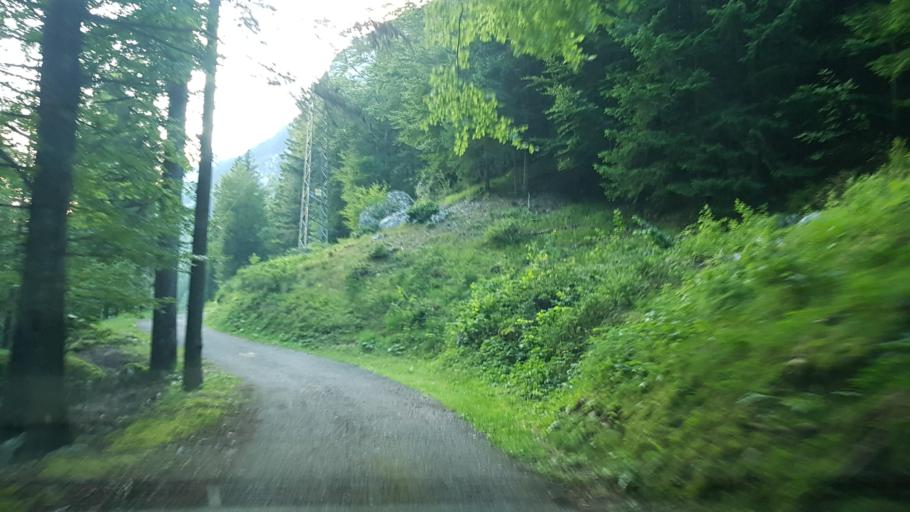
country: SI
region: Bovec
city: Bovec
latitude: 46.3941
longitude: 13.4562
